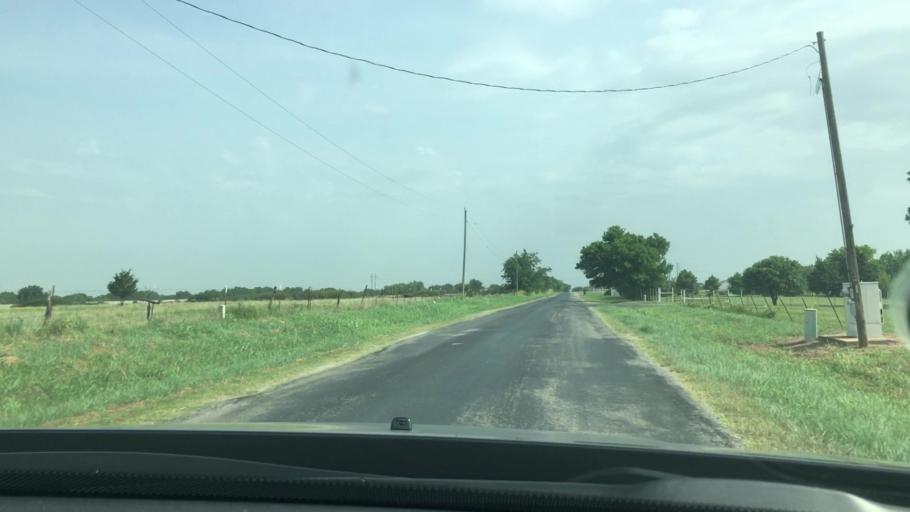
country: US
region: Oklahoma
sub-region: Garvin County
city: Pauls Valley
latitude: 34.8006
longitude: -97.1955
